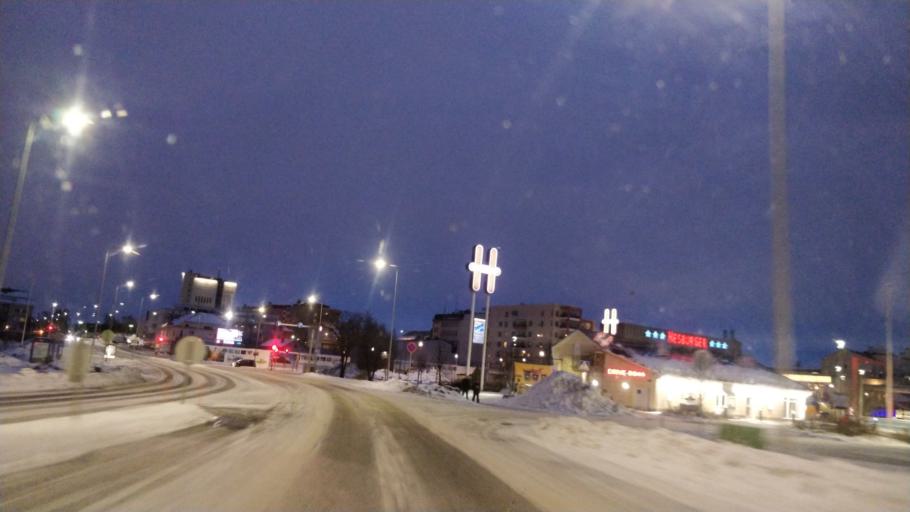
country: FI
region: Lapland
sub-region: Kemi-Tornio
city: Kemi
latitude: 65.7397
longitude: 24.5652
